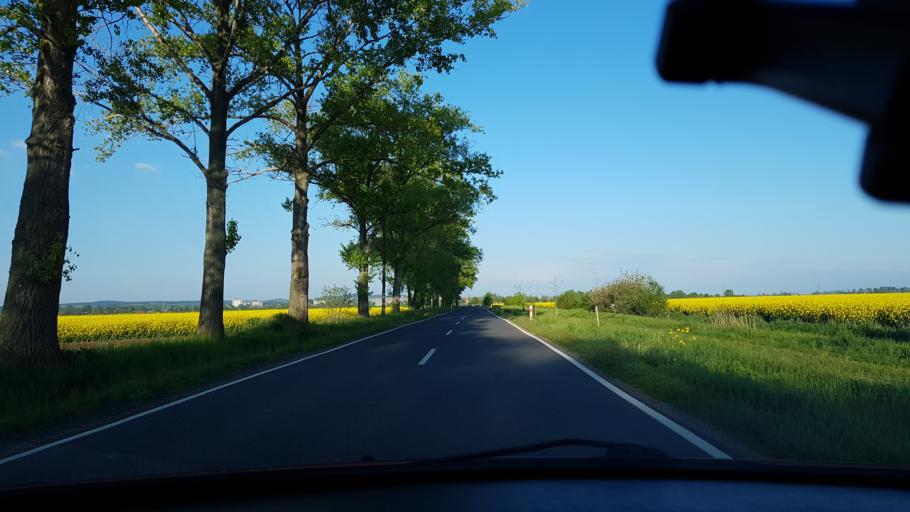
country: PL
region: Lower Silesian Voivodeship
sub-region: Powiat zabkowicki
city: Stoszowice
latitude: 50.5986
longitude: 16.7608
